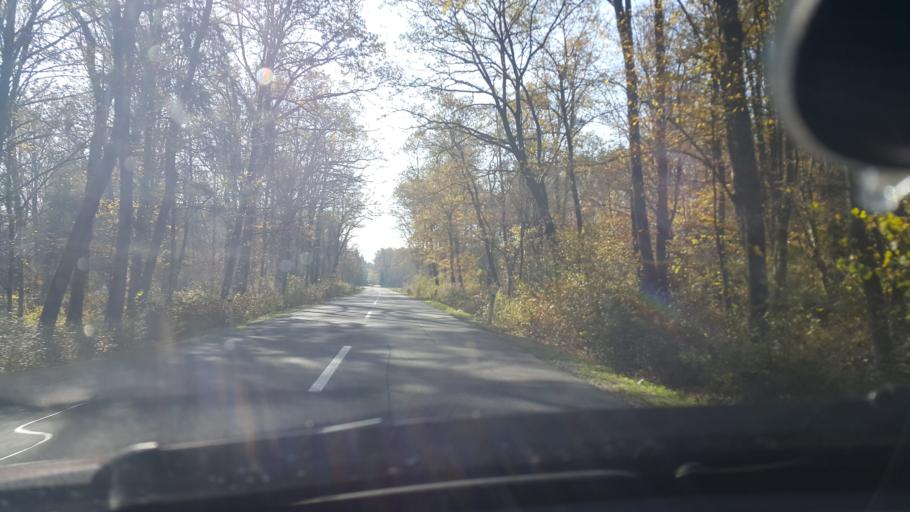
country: SI
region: Brezice
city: Brezice
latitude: 45.9322
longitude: 15.6407
